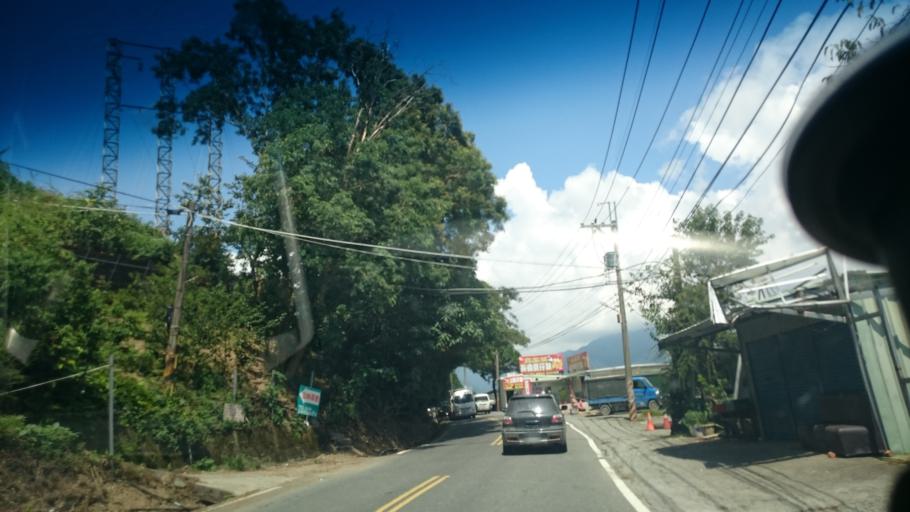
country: TW
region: Taiwan
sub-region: Nantou
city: Puli
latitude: 24.0289
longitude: 121.1441
